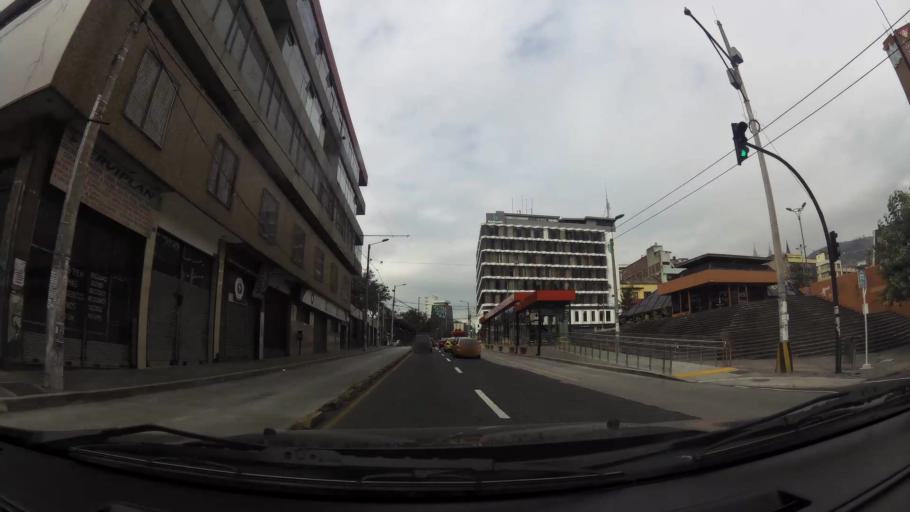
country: EC
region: Pichincha
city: Quito
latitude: -0.2135
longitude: -78.5027
